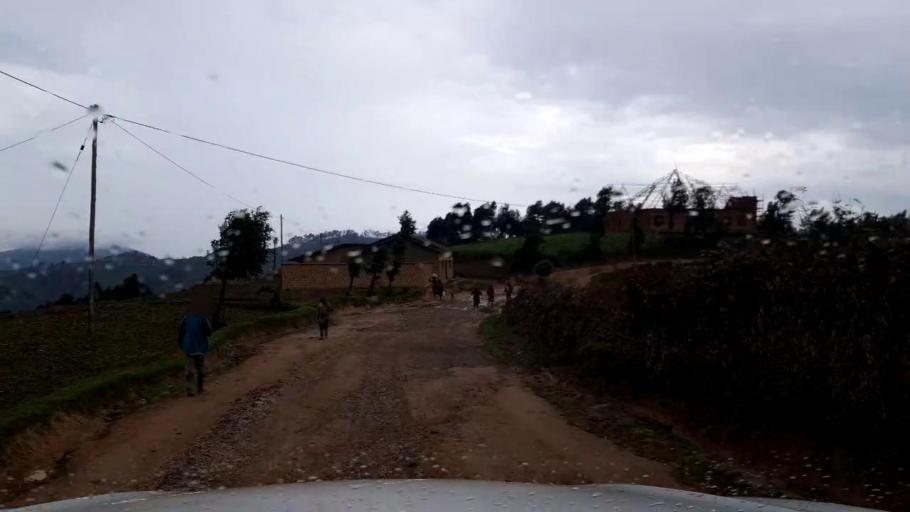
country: RW
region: Western Province
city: Kibuye
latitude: -2.0141
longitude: 29.4712
